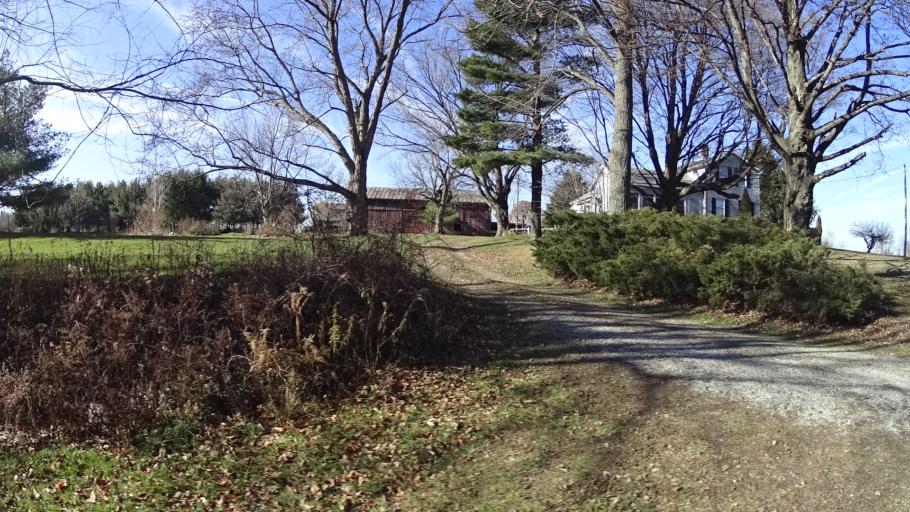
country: US
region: Ohio
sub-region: Lorain County
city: Wellington
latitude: 41.0710
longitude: -82.2795
